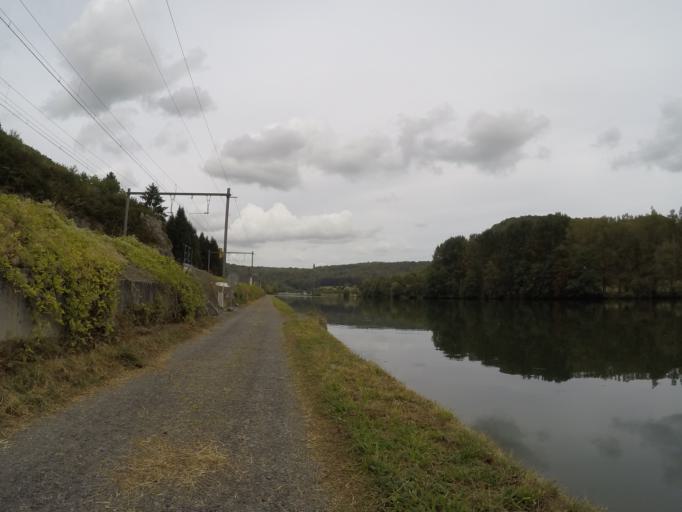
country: BE
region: Wallonia
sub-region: Province de Namur
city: Anhee
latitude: 50.2899
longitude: 4.8922
